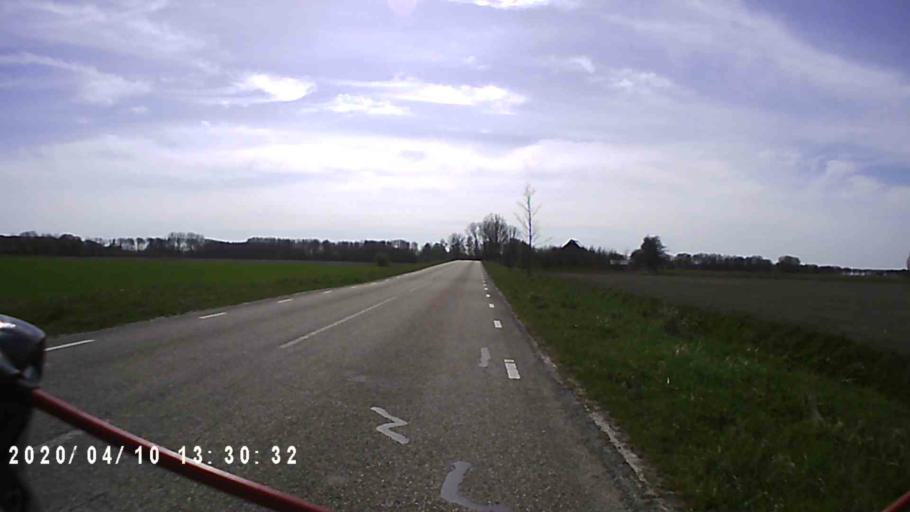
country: NL
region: Groningen
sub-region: Gemeente Zuidhorn
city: Oldehove
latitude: 53.3687
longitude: 6.4197
